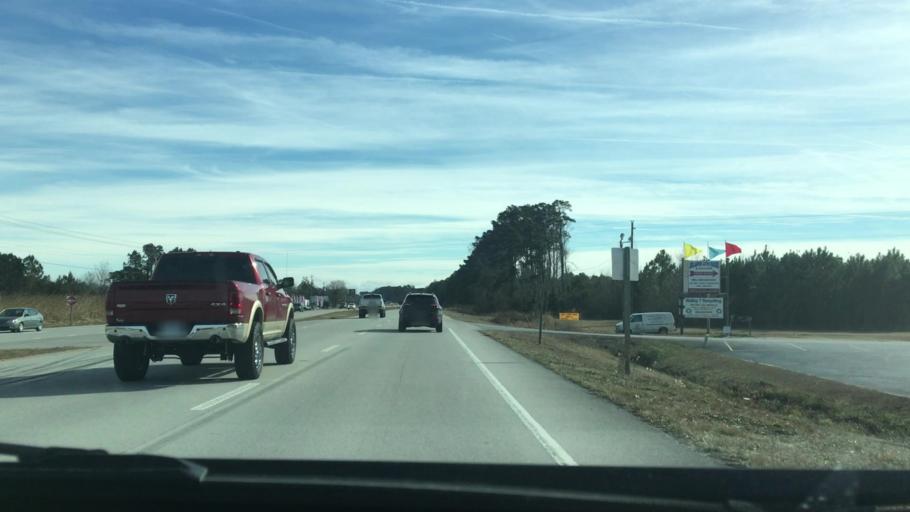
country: US
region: North Carolina
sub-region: Carteret County
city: Newport
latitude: 34.7557
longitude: -76.8469
